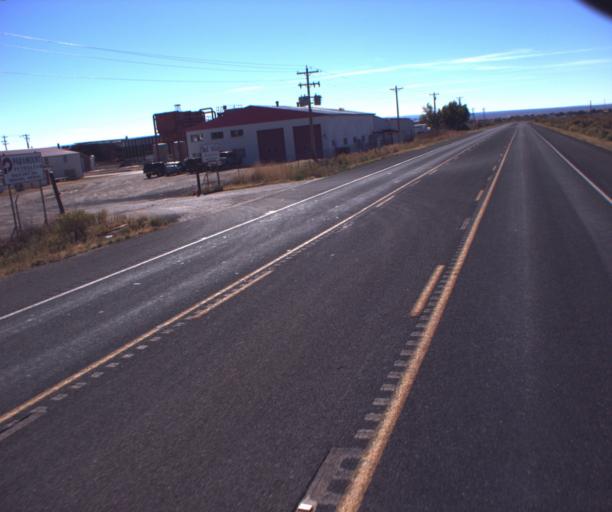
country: US
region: Arizona
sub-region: Coconino County
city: Fredonia
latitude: 36.9719
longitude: -112.5277
